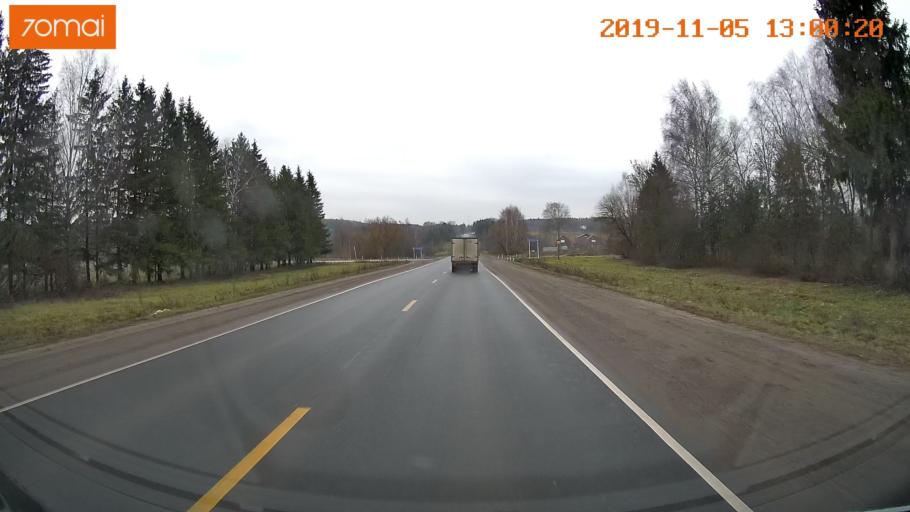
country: RU
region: Ivanovo
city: Kokhma
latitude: 56.9145
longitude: 41.1431
